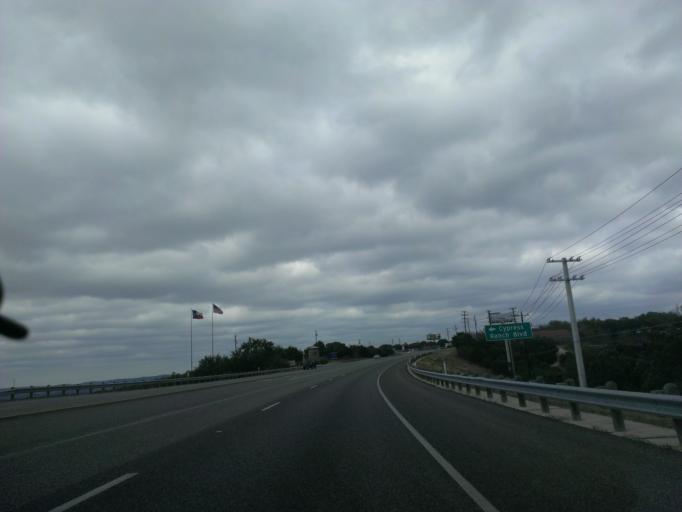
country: US
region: Texas
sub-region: Travis County
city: Briarcliff
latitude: 30.3588
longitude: -98.0688
